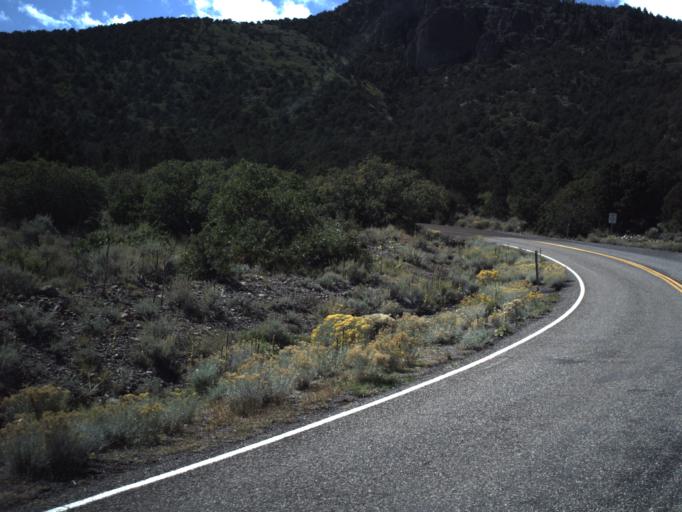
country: US
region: Utah
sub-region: Piute County
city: Junction
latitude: 38.2653
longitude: -112.3042
